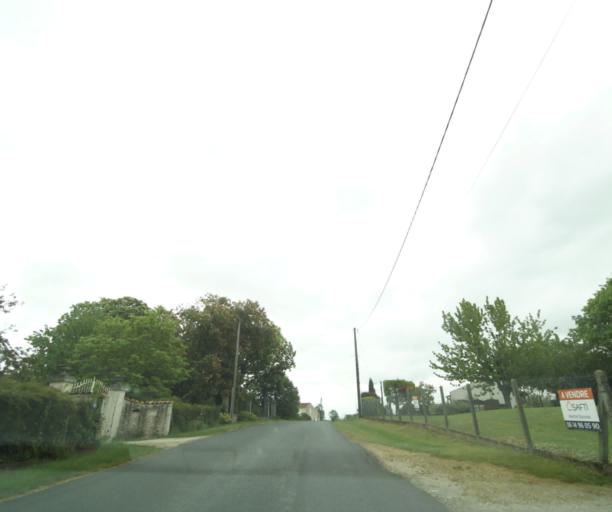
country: FR
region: Poitou-Charentes
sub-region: Departement de la Charente-Maritime
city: Chaniers
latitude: 45.7005
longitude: -0.5474
